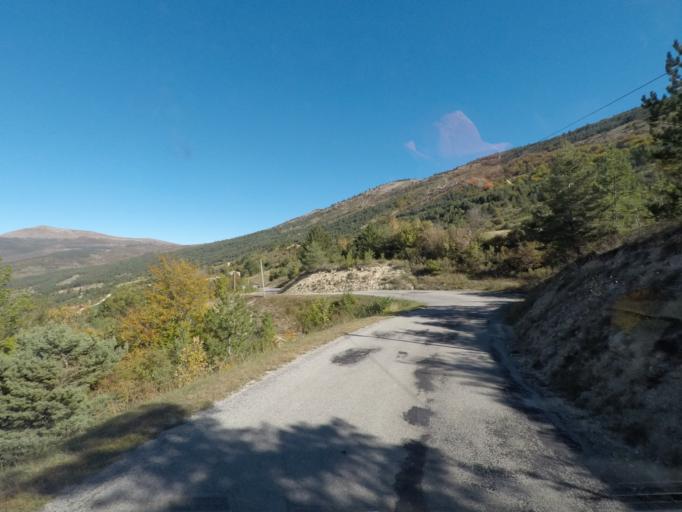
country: FR
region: Rhone-Alpes
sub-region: Departement de la Drome
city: Die
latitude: 44.5407
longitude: 5.3692
